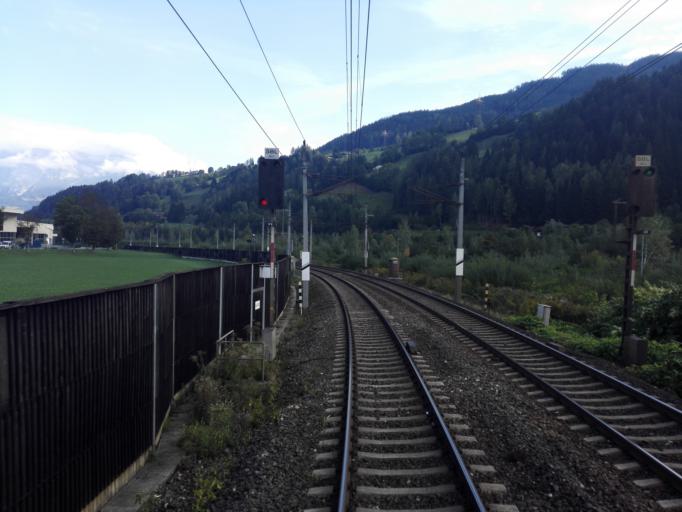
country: AT
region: Salzburg
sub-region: Politischer Bezirk Sankt Johann im Pongau
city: Bischofshofen
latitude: 47.3967
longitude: 13.2246
